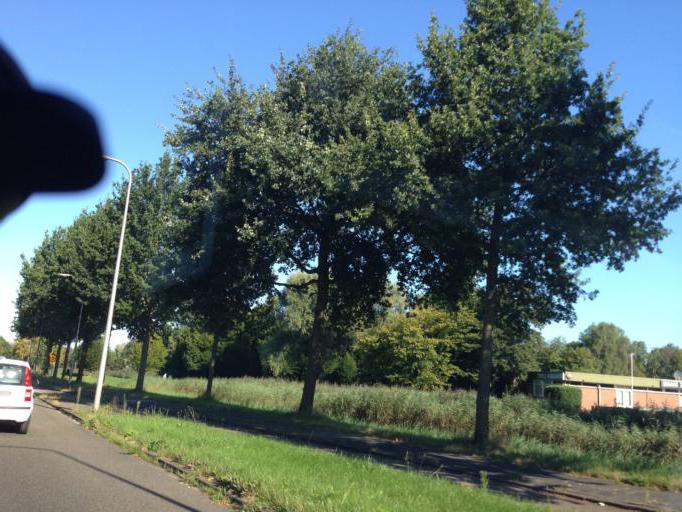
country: NL
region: Overijssel
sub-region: Gemeente Zwolle
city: Zwolle
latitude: 52.5193
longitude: 6.1024
